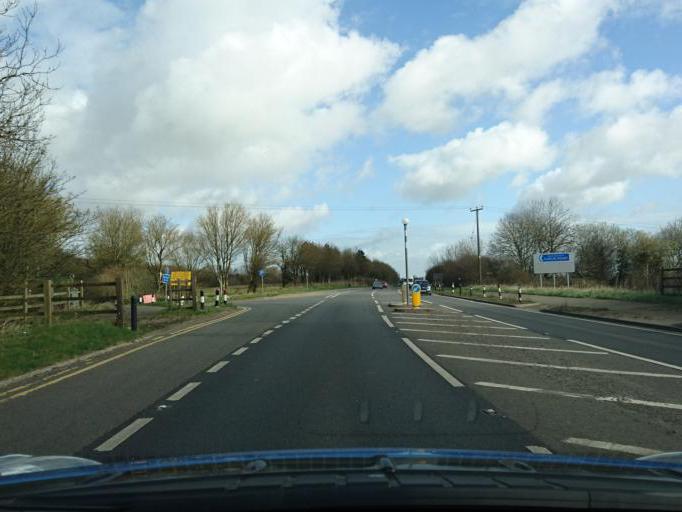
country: GB
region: England
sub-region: South Gloucestershire
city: Hinton
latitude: 51.4965
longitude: -2.3540
